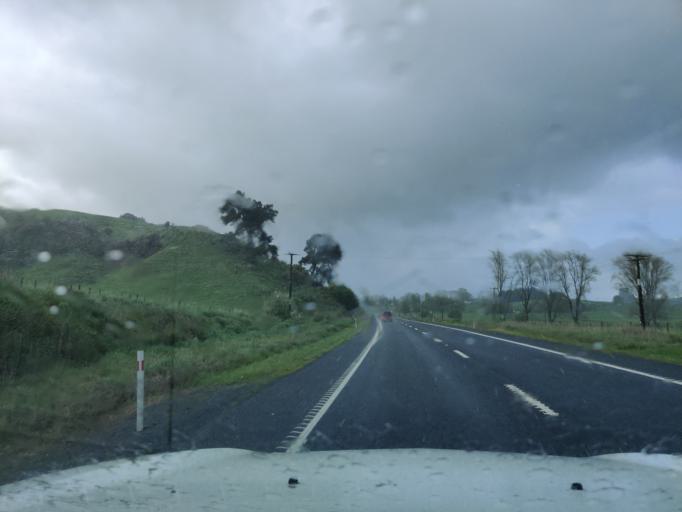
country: NZ
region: Waikato
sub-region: Matamata-Piako District
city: Matamata
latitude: -37.9698
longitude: 175.6911
